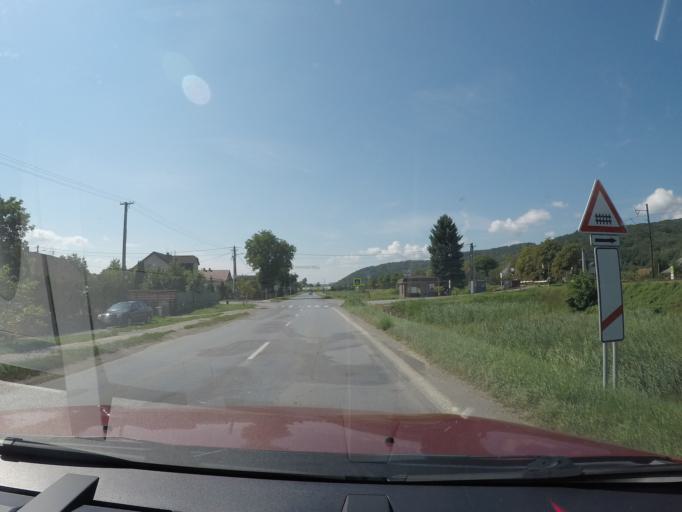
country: SK
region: Presovsky
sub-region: Okres Presov
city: Presov
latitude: 48.9580
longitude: 21.2415
